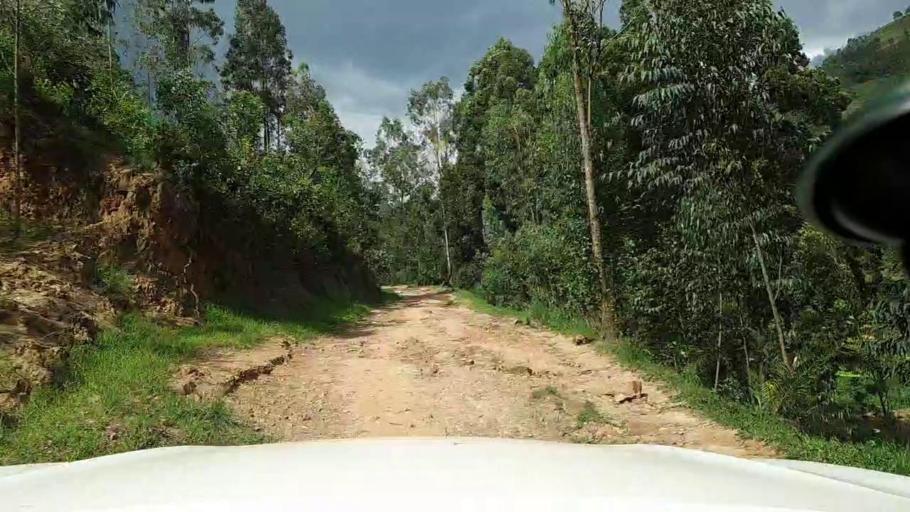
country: RW
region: Southern Province
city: Gitarama
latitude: -1.8239
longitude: 29.8011
